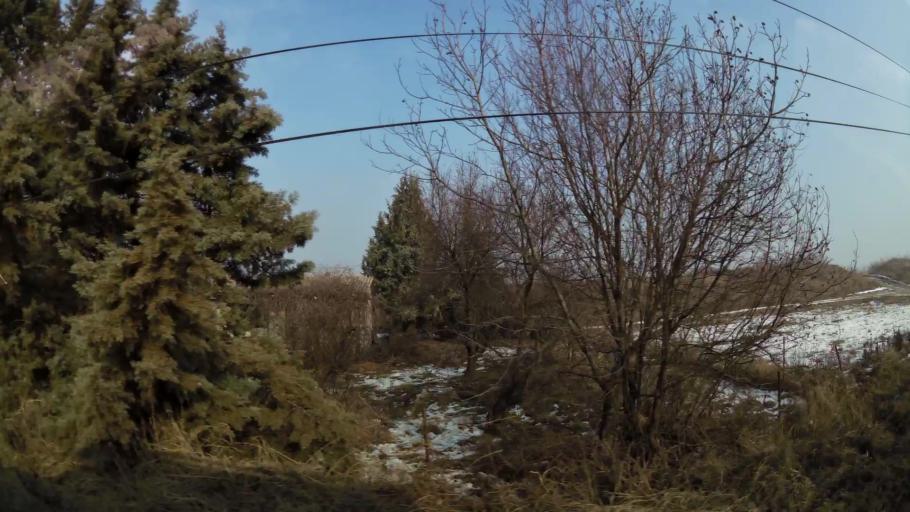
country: MK
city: Kadino
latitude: 41.9799
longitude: 21.5978
